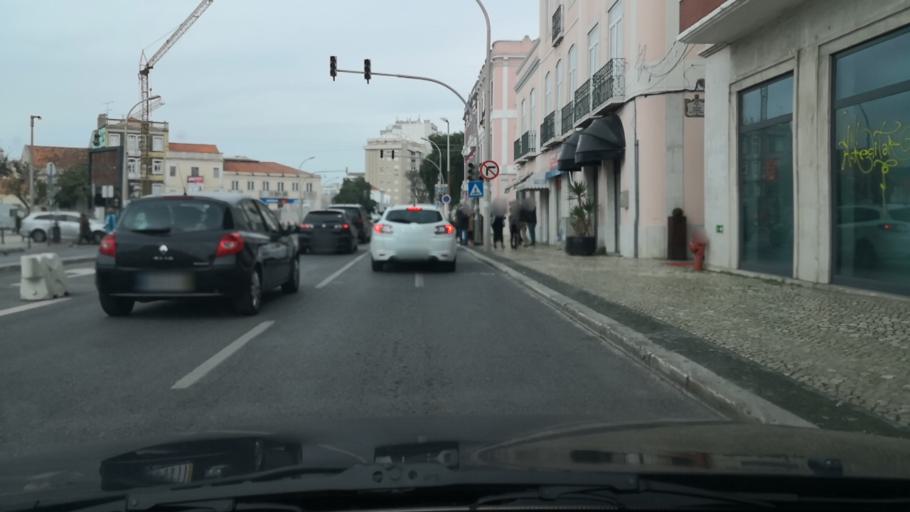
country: PT
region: Setubal
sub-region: Setubal
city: Setubal
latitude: 38.5242
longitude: -8.8943
